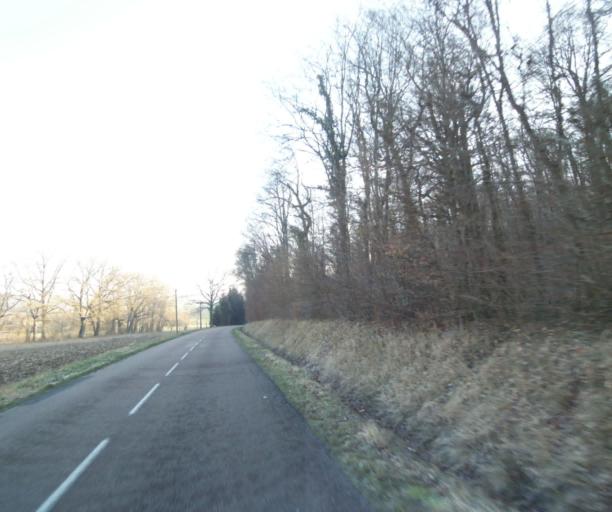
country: FR
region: Champagne-Ardenne
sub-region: Departement de la Haute-Marne
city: Bienville
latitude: 48.5591
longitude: 5.0846
